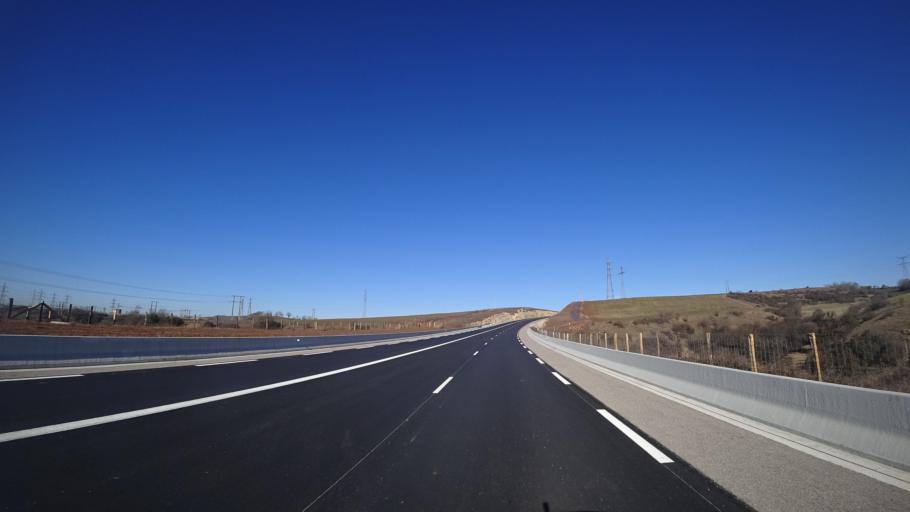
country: FR
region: Midi-Pyrenees
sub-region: Departement de l'Aveyron
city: Sebazac-Concoures
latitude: 44.3859
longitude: 2.6149
